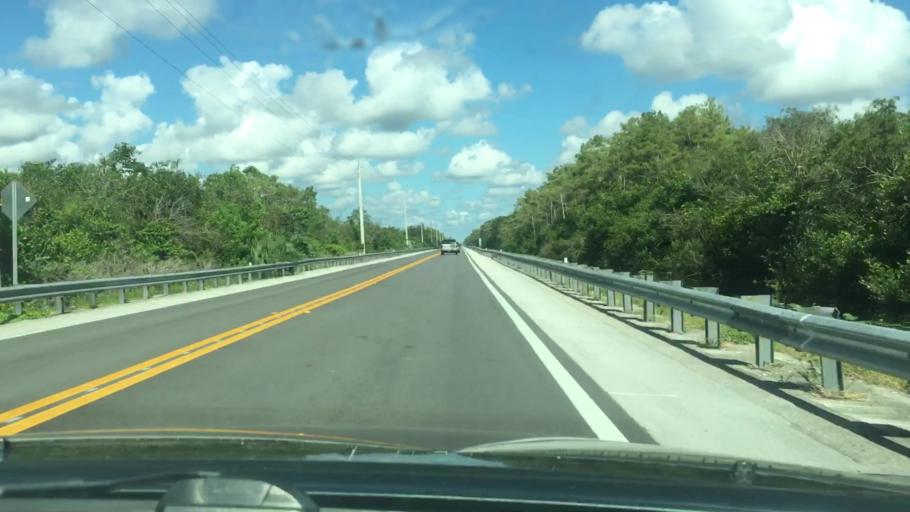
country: US
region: Florida
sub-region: Miami-Dade County
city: Kendall West
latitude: 25.7641
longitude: -80.8306
